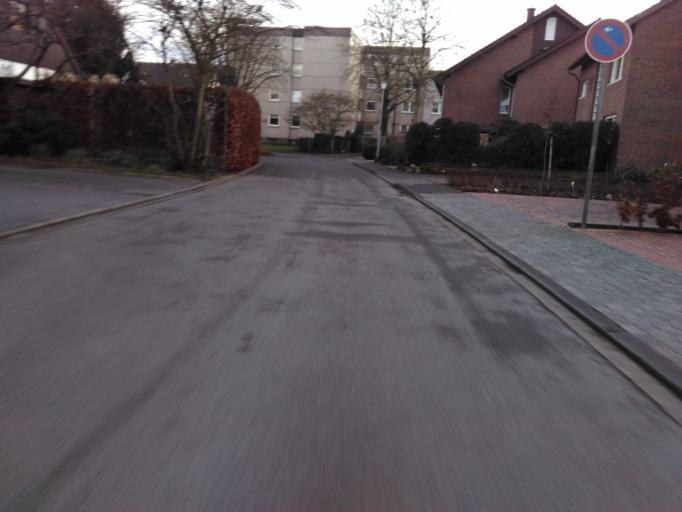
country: DE
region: North Rhine-Westphalia
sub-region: Regierungsbezirk Detmold
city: Verl
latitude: 51.8797
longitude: 8.5069
